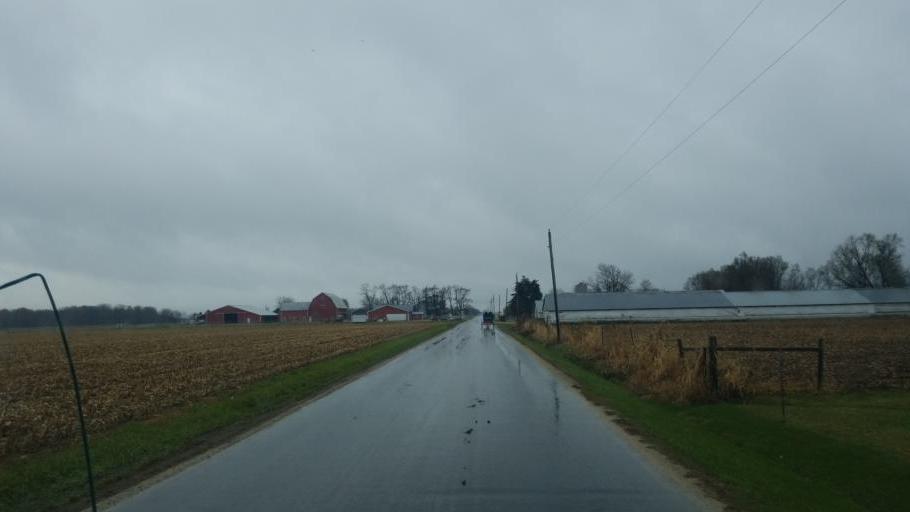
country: US
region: Indiana
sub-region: Adams County
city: Berne
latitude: 40.7061
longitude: -84.9173
